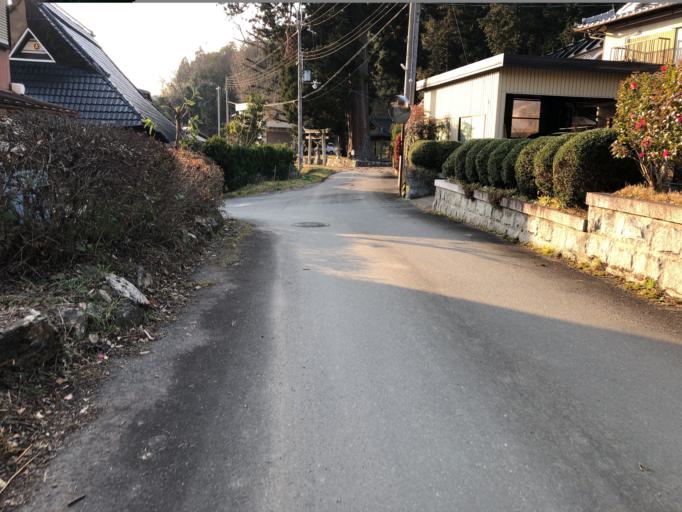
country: JP
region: Kyoto
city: Kameoka
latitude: 35.0596
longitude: 135.4839
